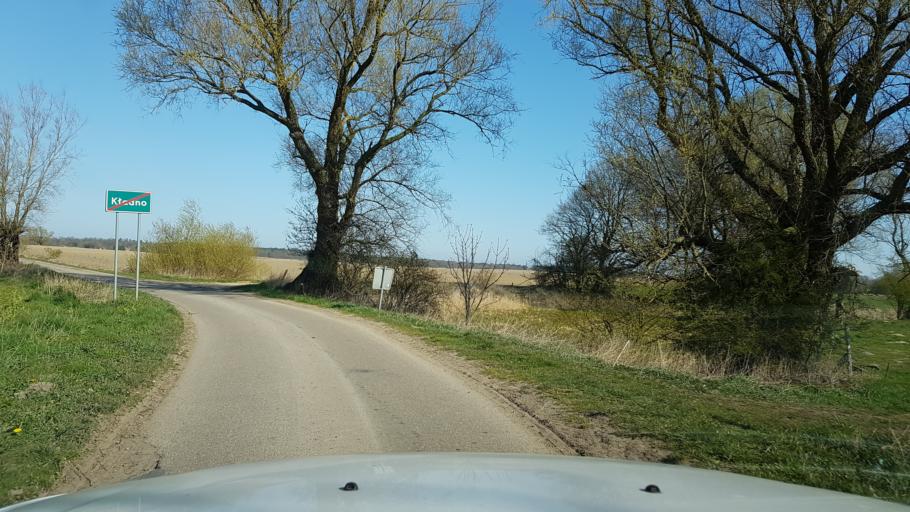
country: PL
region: West Pomeranian Voivodeship
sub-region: Powiat kolobrzeski
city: Ustronie Morskie
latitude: 54.2190
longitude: 15.8490
